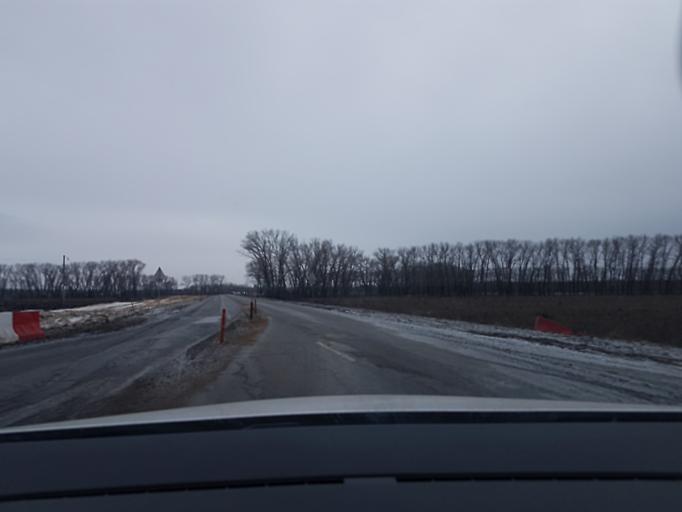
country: RU
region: Tambov
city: Zavoronezhskoye
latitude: 52.9487
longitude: 40.5866
